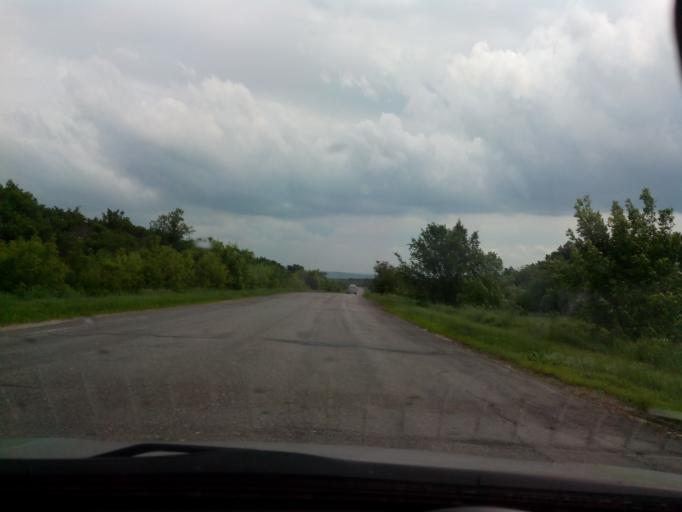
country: RU
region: Volgograd
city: Mikhaylovka
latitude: 49.9963
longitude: 43.1118
